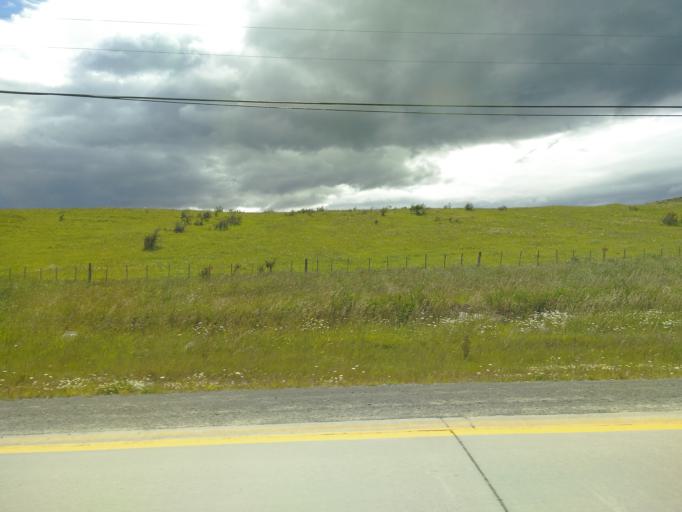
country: CL
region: Magallanes
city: Puerto Natales
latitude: -51.6972
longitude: -72.5247
